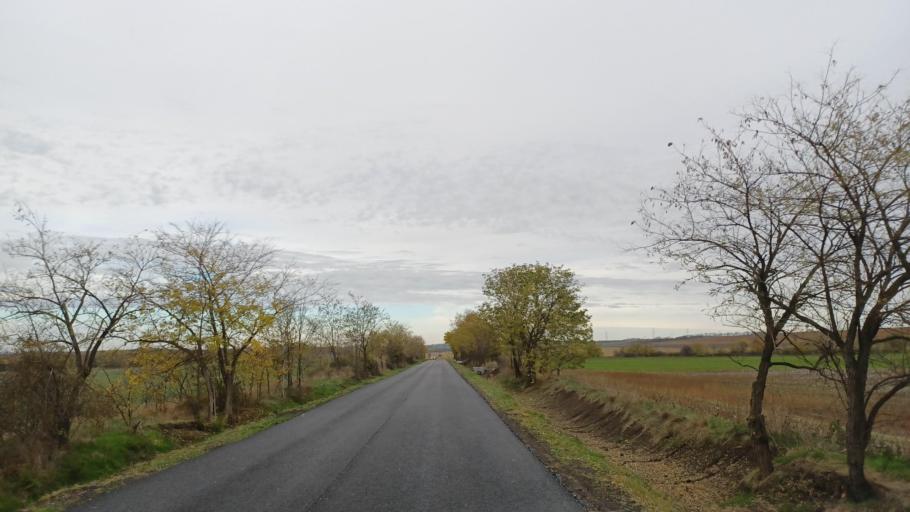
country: HU
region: Tolna
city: Tengelic
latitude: 46.5471
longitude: 18.7520
